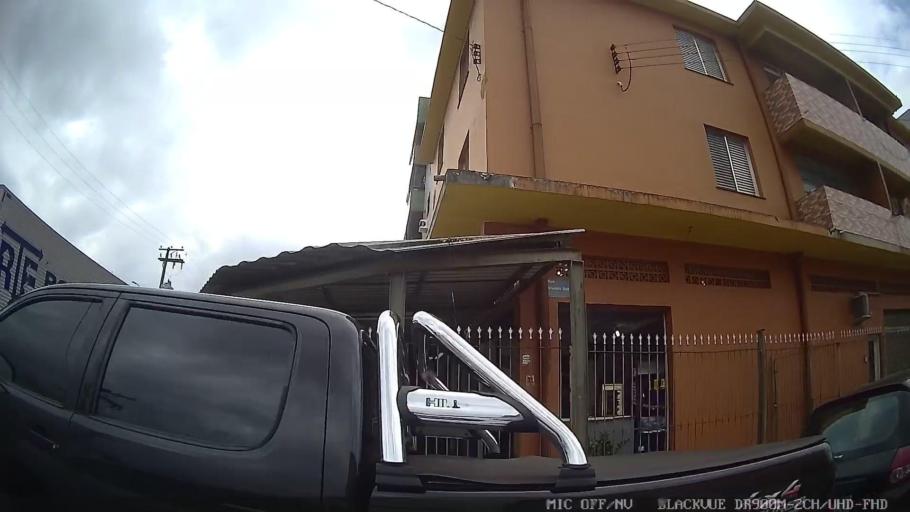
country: BR
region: Sao Paulo
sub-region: Guaruja
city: Guaruja
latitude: -23.9912
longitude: -46.2903
